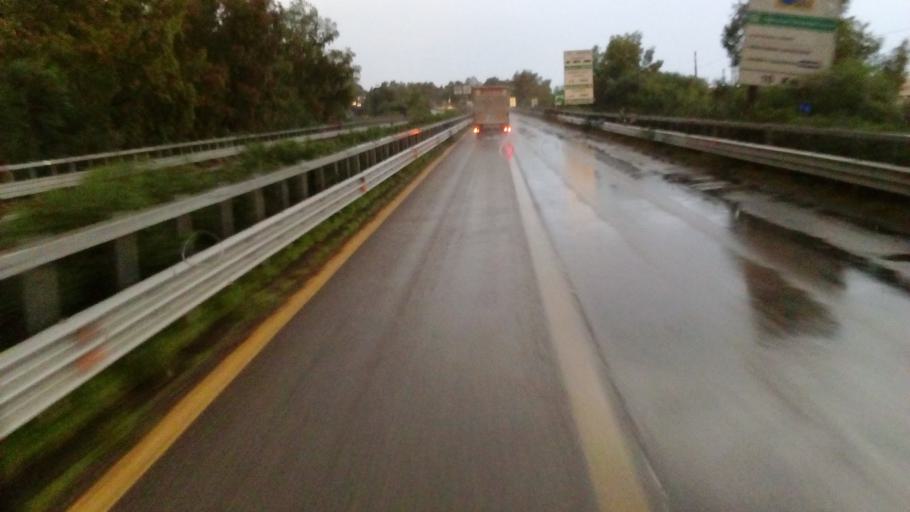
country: IT
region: Sicily
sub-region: Messina
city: Larderia
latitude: 38.1179
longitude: 15.5135
